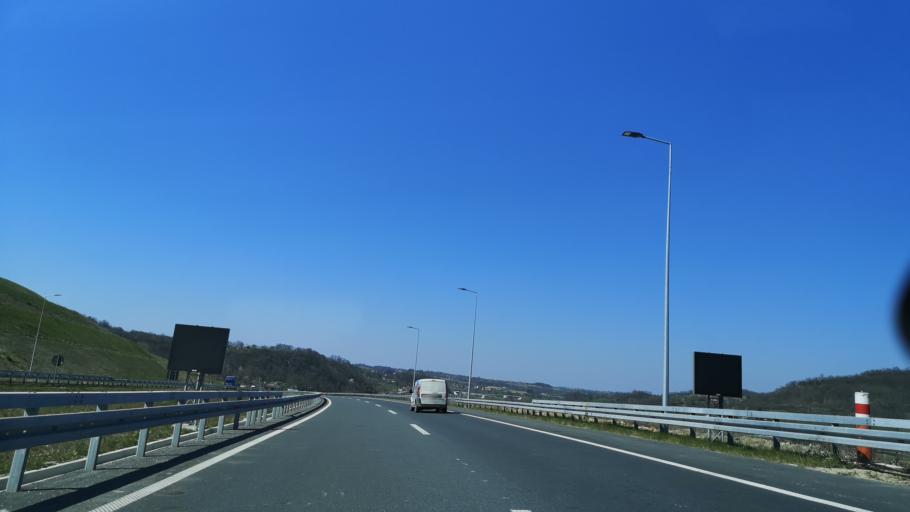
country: RS
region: Central Serbia
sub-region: Kolubarski Okrug
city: Ljig
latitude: 44.2126
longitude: 20.2623
